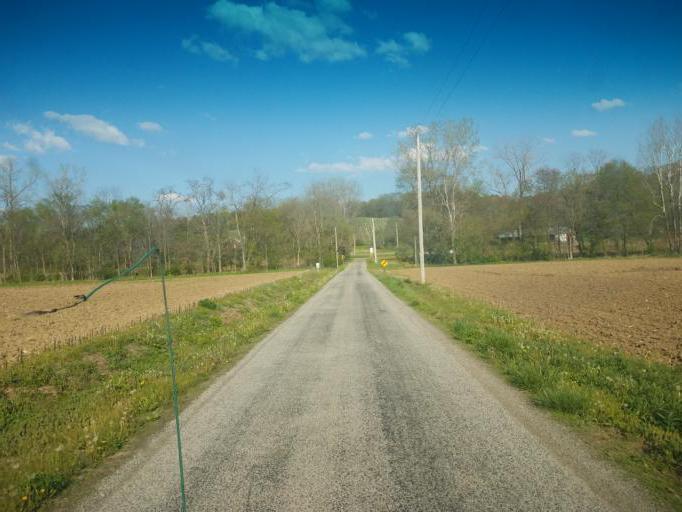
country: US
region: Ohio
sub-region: Wayne County
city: Shreve
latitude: 40.6860
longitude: -81.9457
